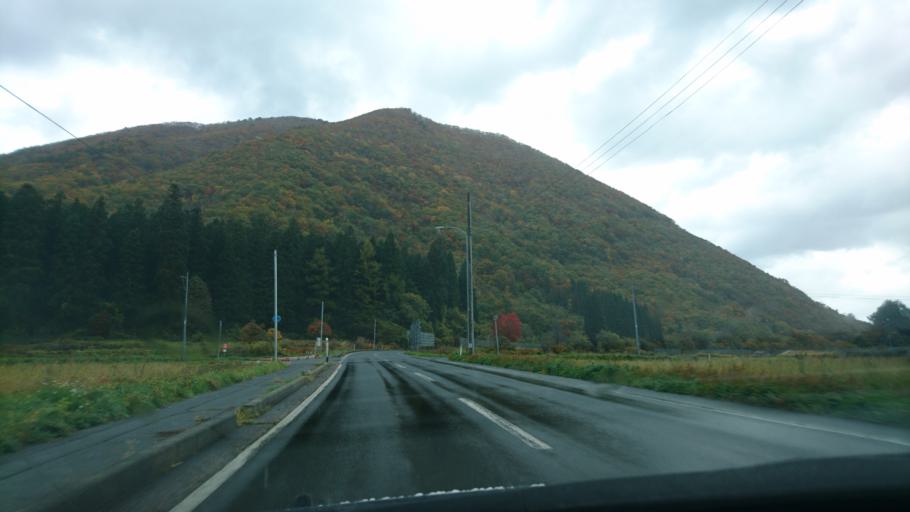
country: JP
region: Iwate
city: Shizukuishi
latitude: 39.6055
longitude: 140.9314
